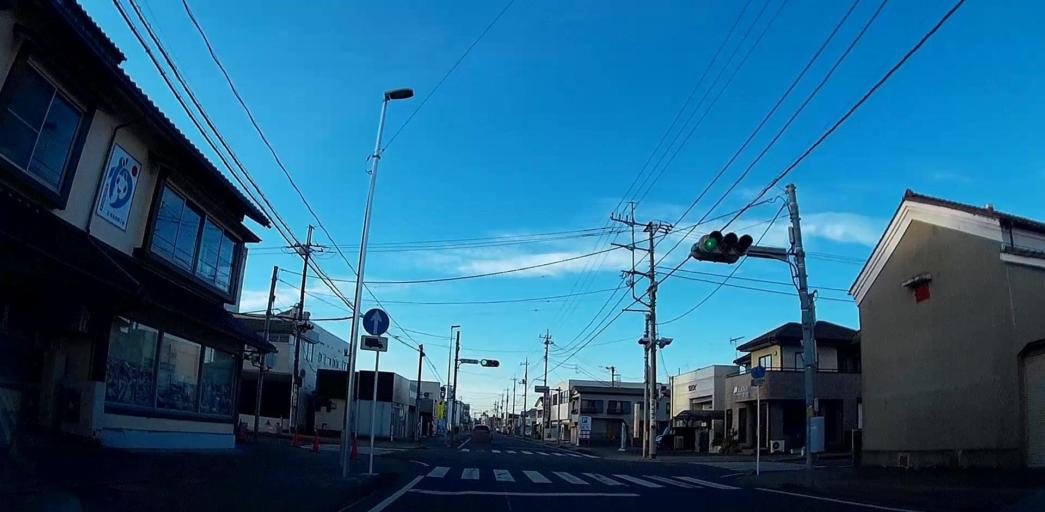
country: JP
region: Chiba
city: Omigawa
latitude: 35.8527
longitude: 140.6082
